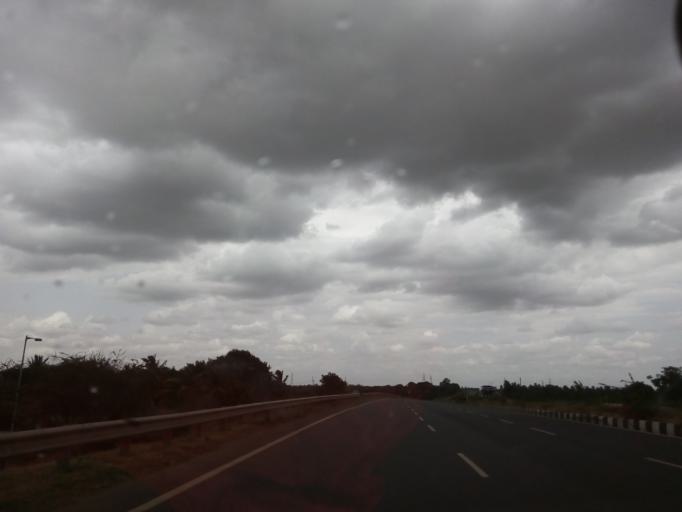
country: IN
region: Karnataka
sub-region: Chitradurga
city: Hiriyur
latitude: 14.0041
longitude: 76.5877
